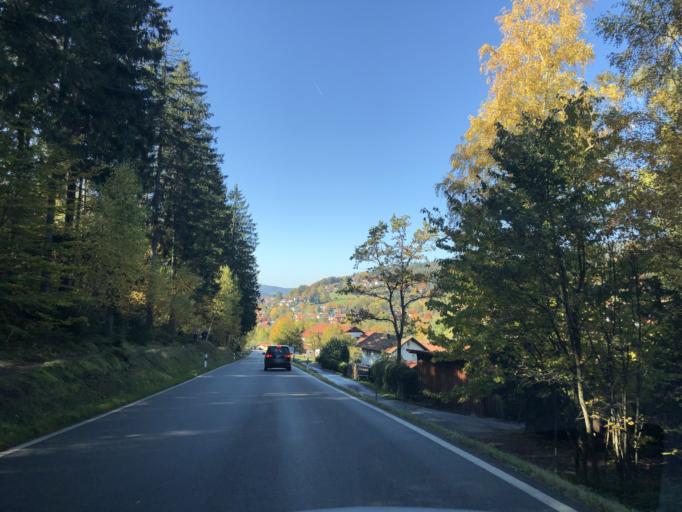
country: DE
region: Bavaria
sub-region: Lower Bavaria
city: Bodenmais
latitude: 49.0663
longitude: 13.1156
